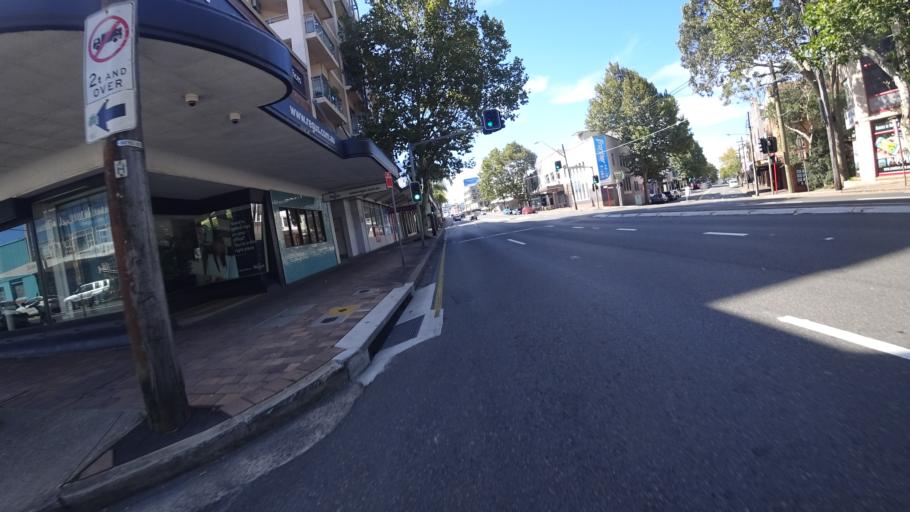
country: AU
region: New South Wales
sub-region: North Sydney
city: Crows Nest
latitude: -33.8292
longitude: 151.2017
